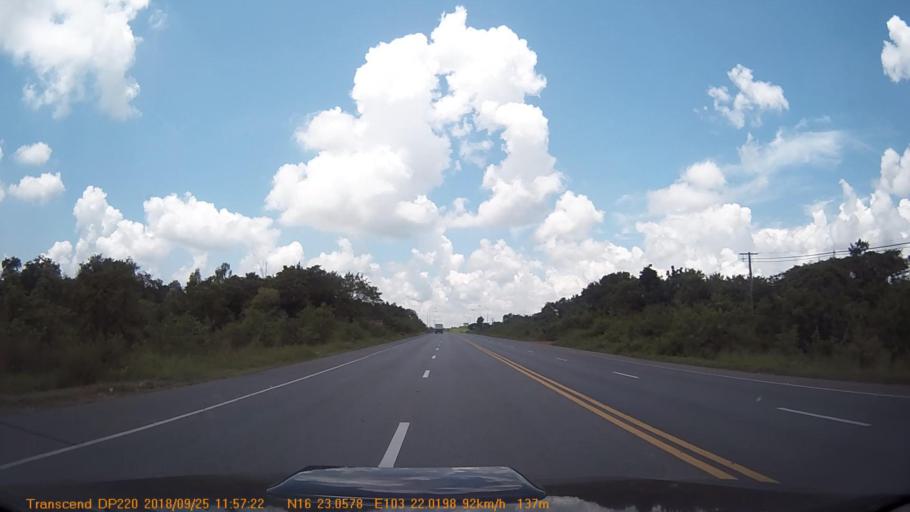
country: TH
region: Kalasin
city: Yang Talat
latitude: 16.3843
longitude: 103.3670
